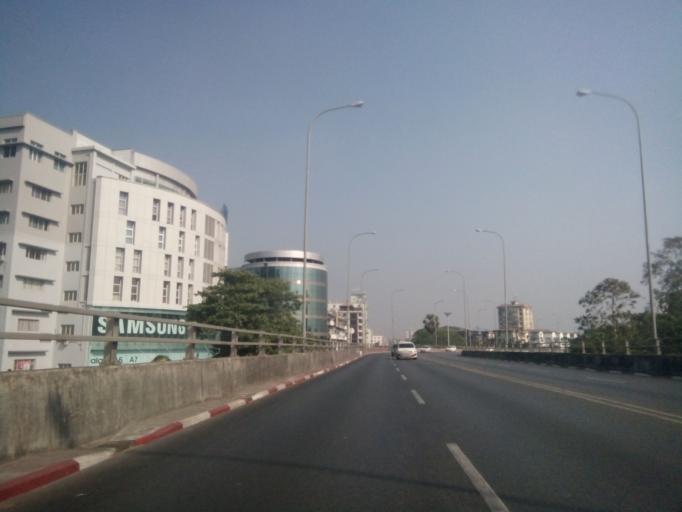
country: MM
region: Yangon
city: Yangon
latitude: 16.8255
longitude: 96.1309
